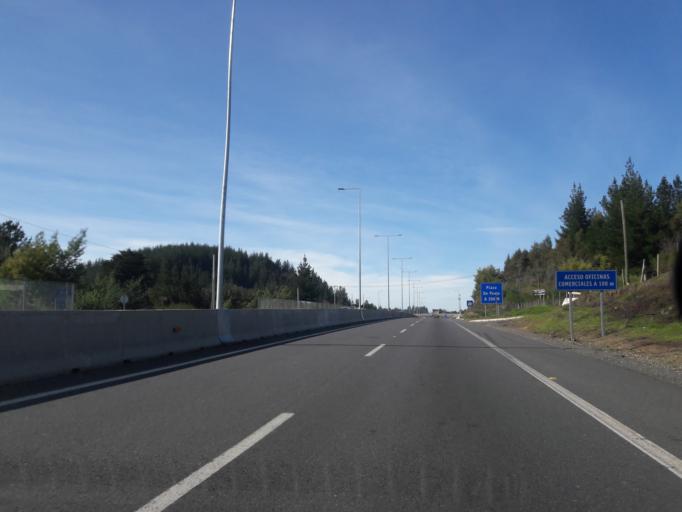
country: CL
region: Biobio
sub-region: Provincia de Biobio
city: Yumbel
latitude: -36.9592
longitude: -72.7364
